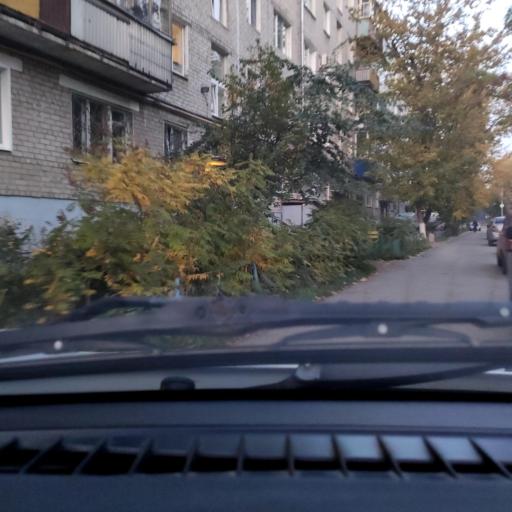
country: RU
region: Samara
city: Zhigulevsk
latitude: 53.4834
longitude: 49.4849
